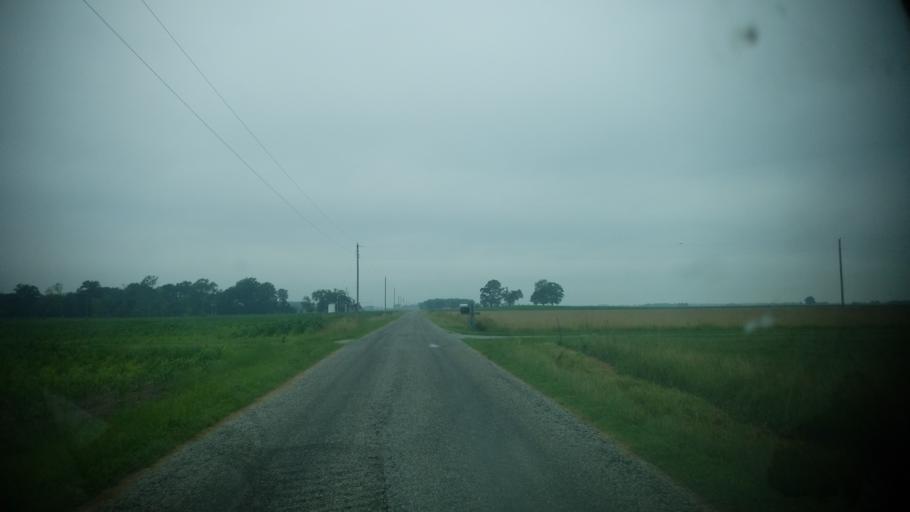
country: US
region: Illinois
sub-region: Clay County
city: Flora
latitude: 38.5736
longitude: -88.4061
